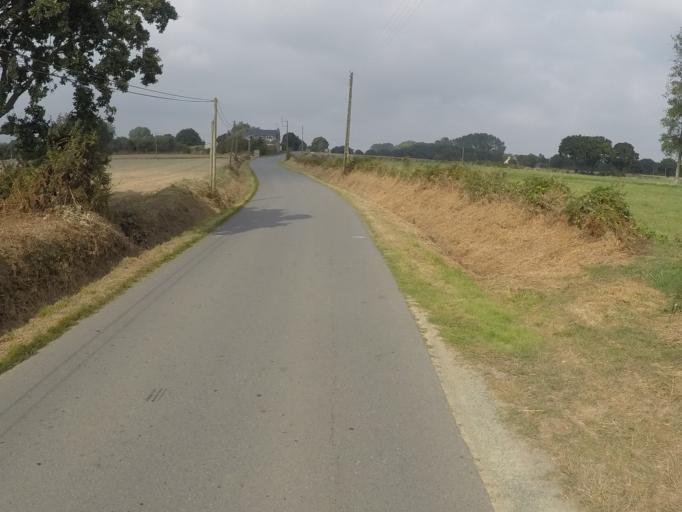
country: FR
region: Brittany
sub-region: Departement des Cotes-d'Armor
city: Pommerit-le-Vicomte
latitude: 48.5838
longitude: -3.0709
